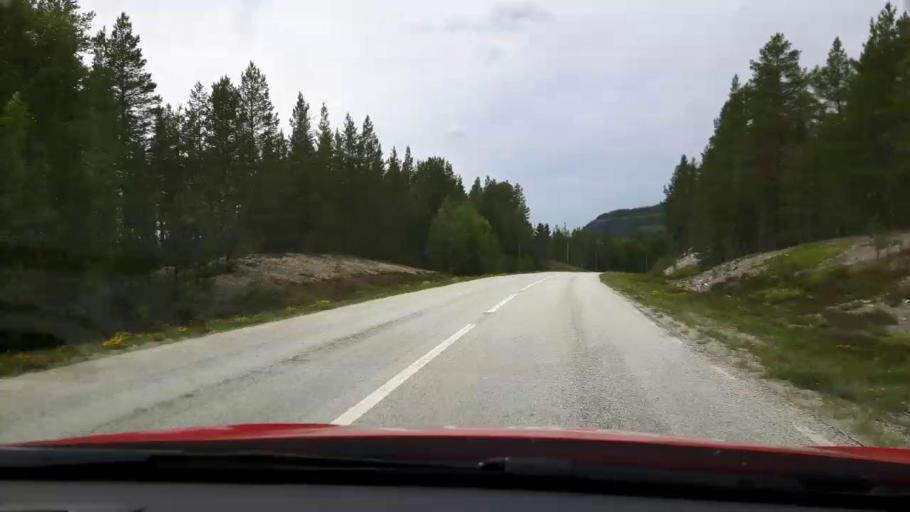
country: SE
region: Jaemtland
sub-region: Harjedalens Kommun
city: Sveg
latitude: 62.4113
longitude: 13.6463
